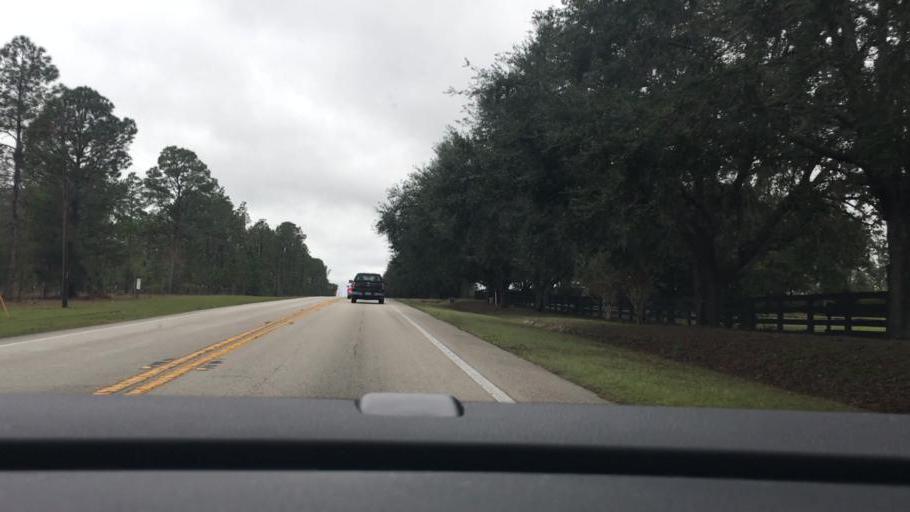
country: US
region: Florida
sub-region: Lake County
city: Mount Plymouth
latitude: 28.8518
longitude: -81.5421
